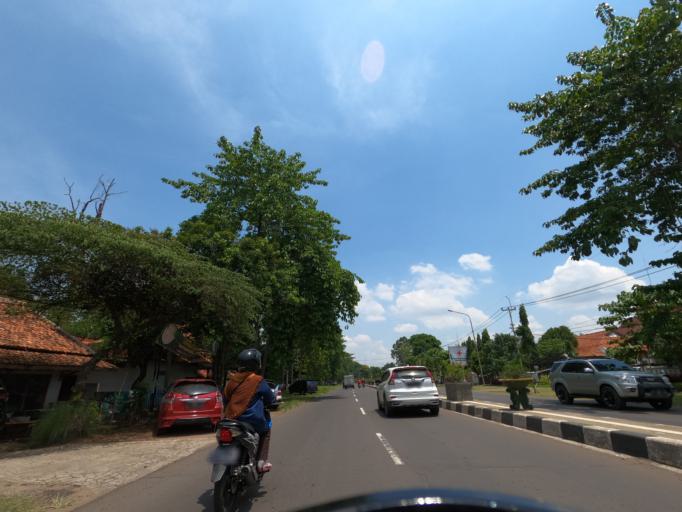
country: ID
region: West Java
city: Pamanukan
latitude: -6.5553
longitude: 107.7619
